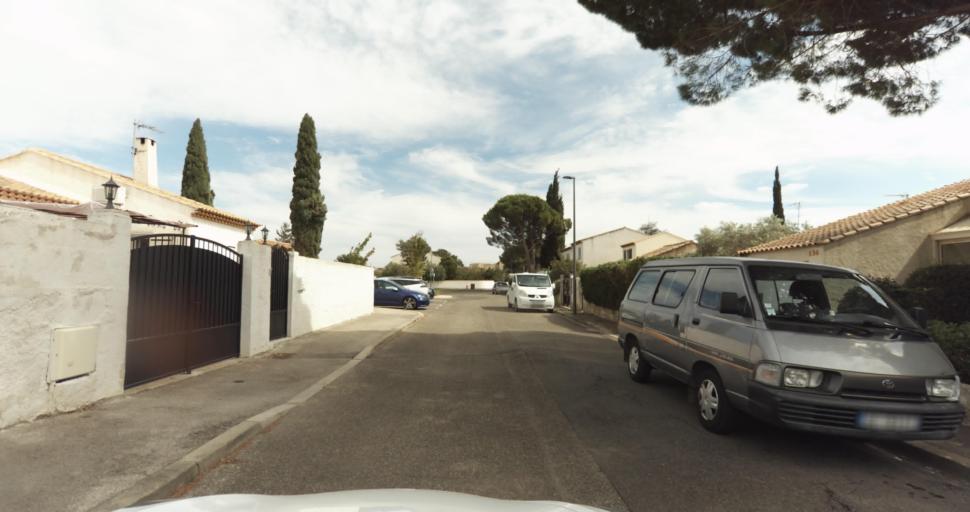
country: FR
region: Provence-Alpes-Cote d'Azur
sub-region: Departement des Bouches-du-Rhone
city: Miramas
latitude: 43.5761
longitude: 4.9928
